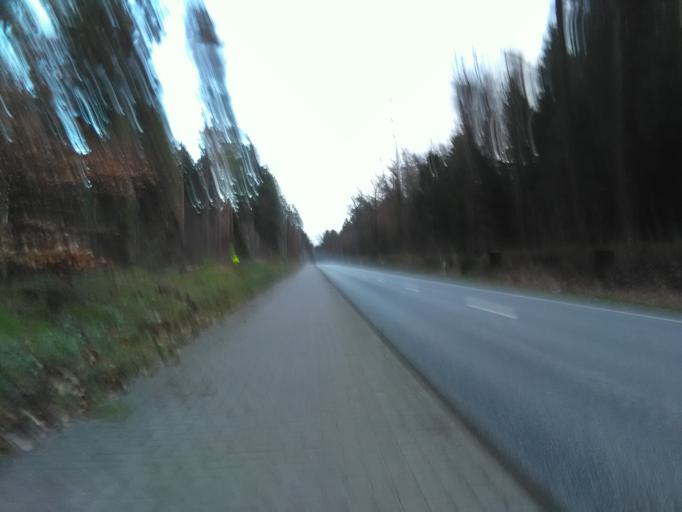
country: DE
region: Schleswig-Holstein
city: Norderstedt
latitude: 53.7208
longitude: 9.9668
